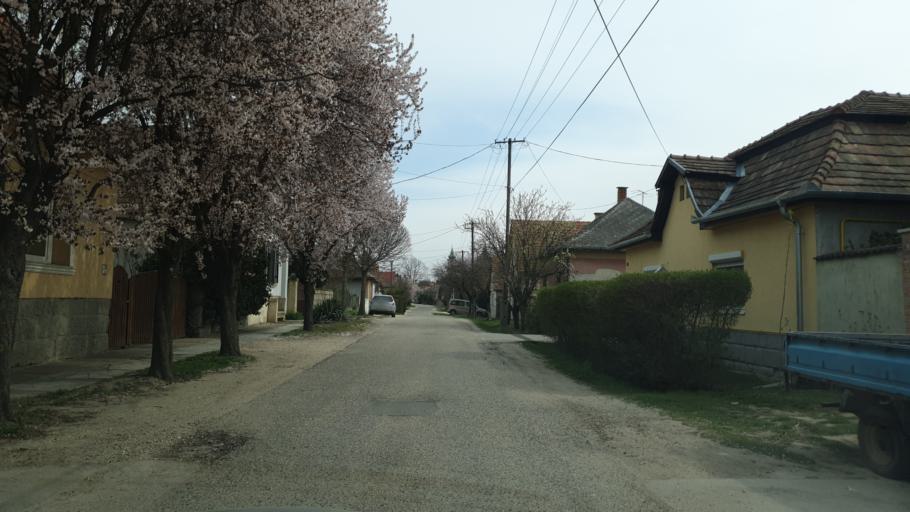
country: HU
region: Fejer
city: Etyek
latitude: 47.4482
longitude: 18.7471
